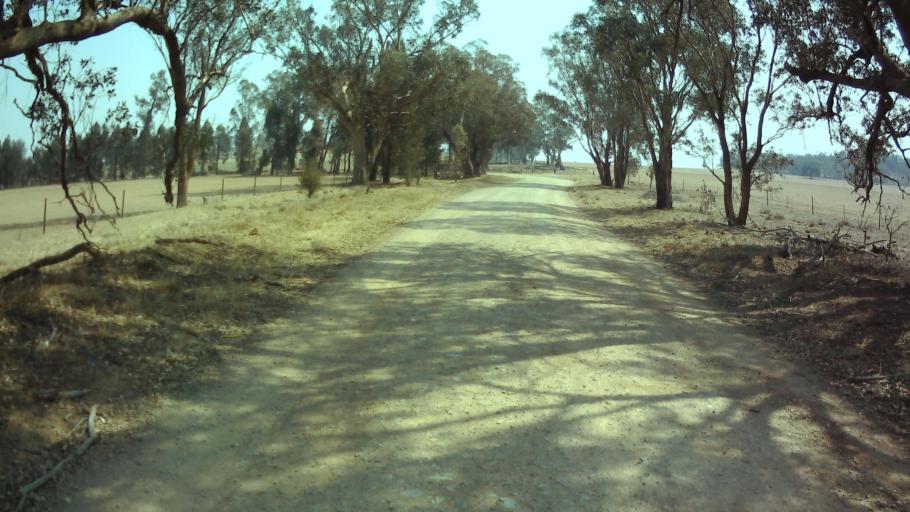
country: AU
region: New South Wales
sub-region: Weddin
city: Grenfell
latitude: -33.6475
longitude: 148.2702
